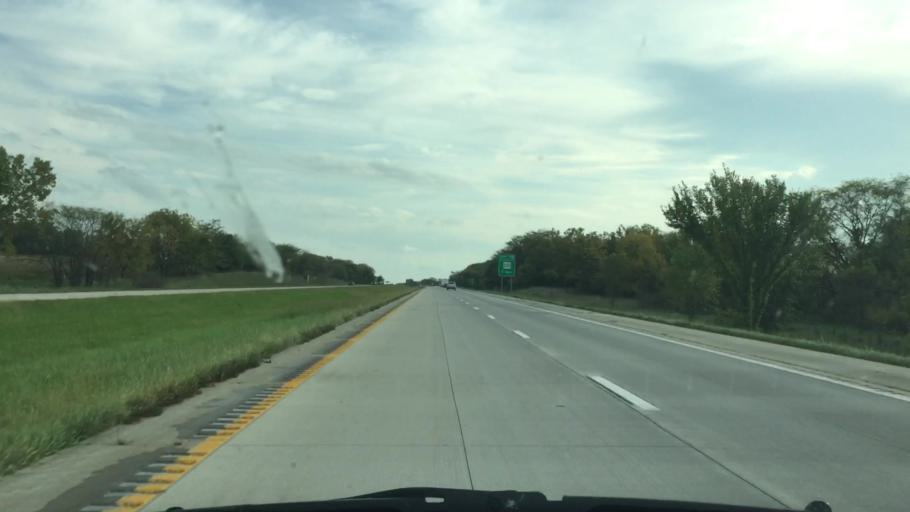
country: US
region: Missouri
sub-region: Daviess County
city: Gallatin
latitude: 40.0143
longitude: -94.0964
